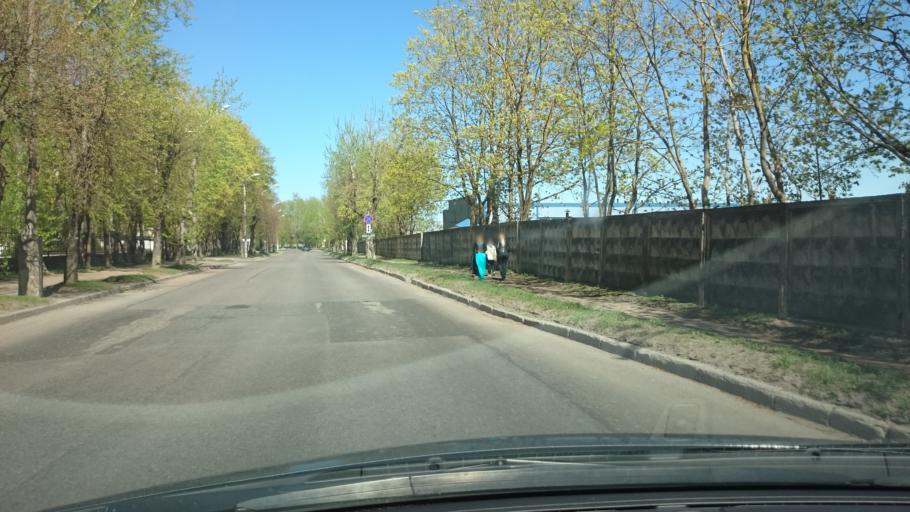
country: EE
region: Ida-Virumaa
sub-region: Narva linn
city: Narva
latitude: 59.3642
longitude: 28.2001
